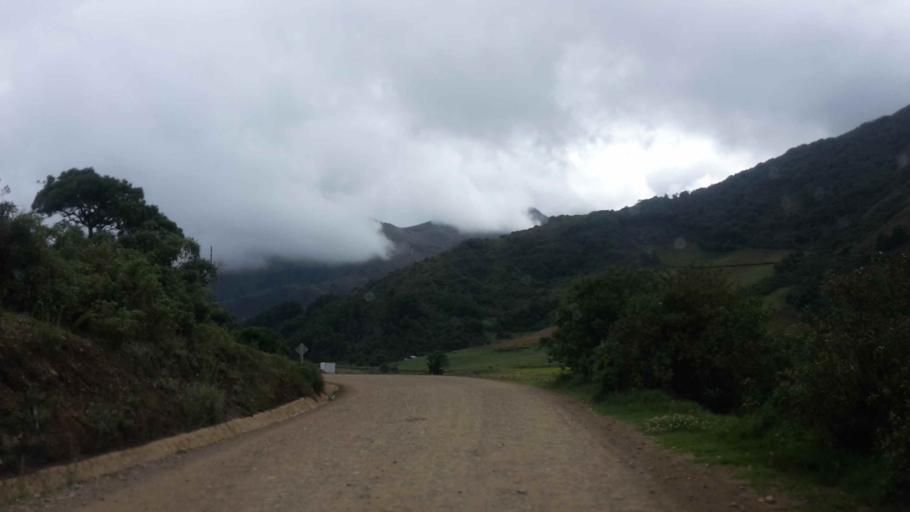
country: BO
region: Cochabamba
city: Totora
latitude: -17.5742
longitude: -65.2859
